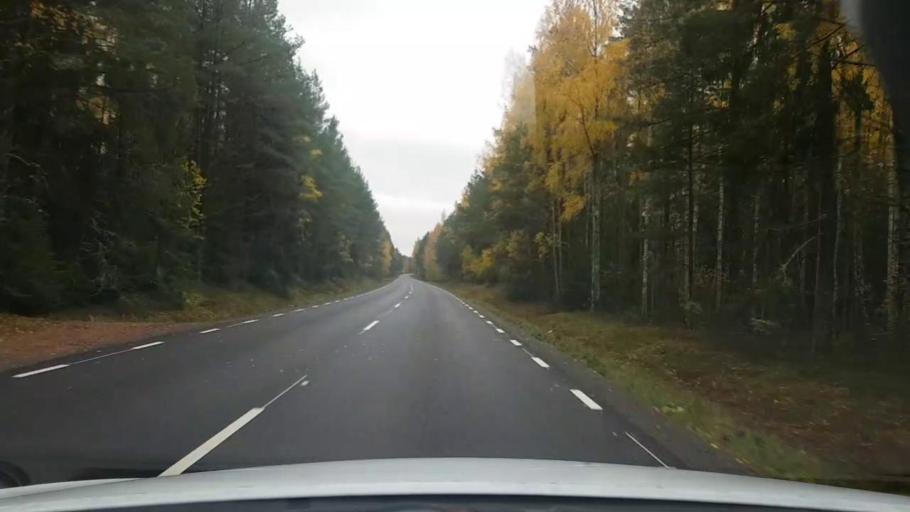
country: SE
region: OErebro
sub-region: Laxa Kommun
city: Laxa
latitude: 58.8016
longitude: 14.5424
